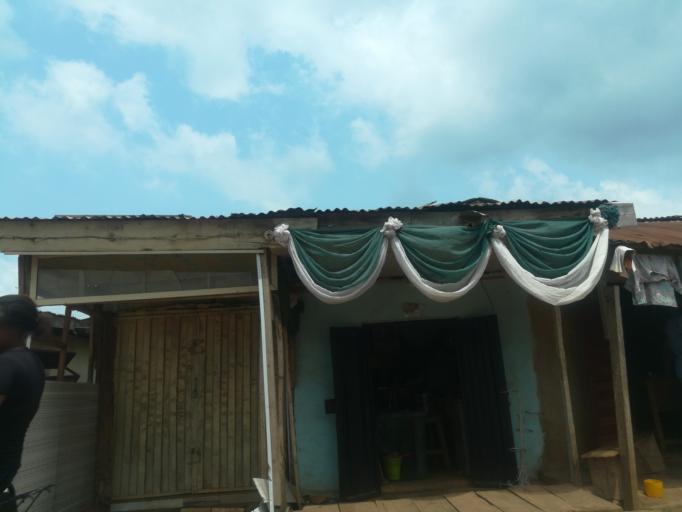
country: NG
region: Oyo
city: Moniya
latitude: 7.4549
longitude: 3.9608
